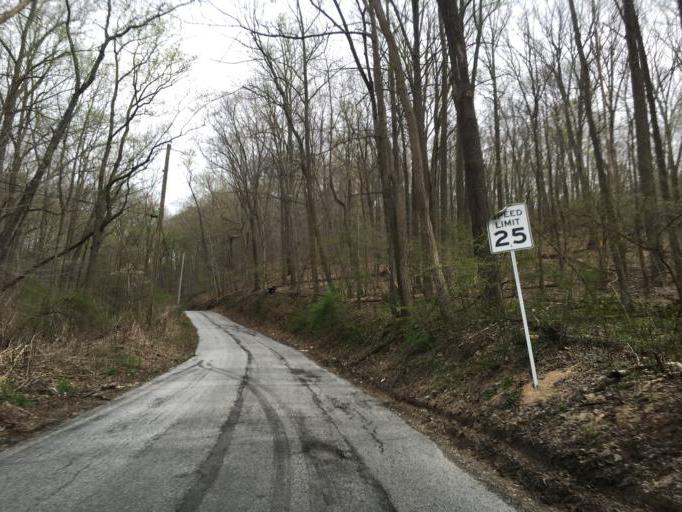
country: US
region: Maryland
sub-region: Baltimore County
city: Hunt Valley
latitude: 39.5050
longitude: -76.6149
